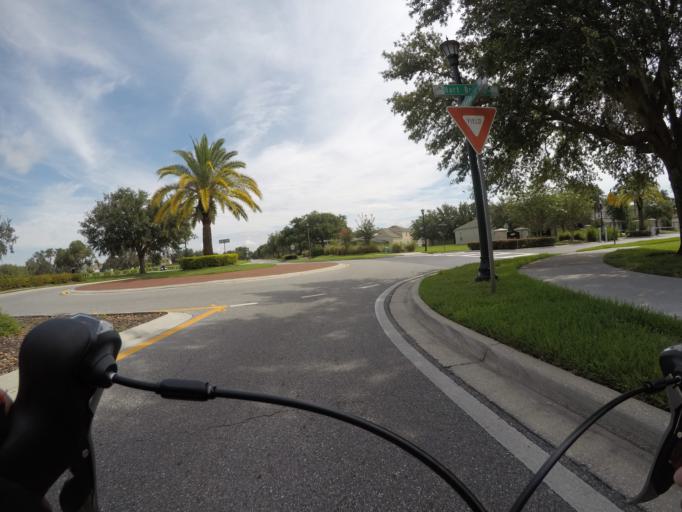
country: US
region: Florida
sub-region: Orange County
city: Meadow Woods
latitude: 28.4021
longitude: -81.2215
